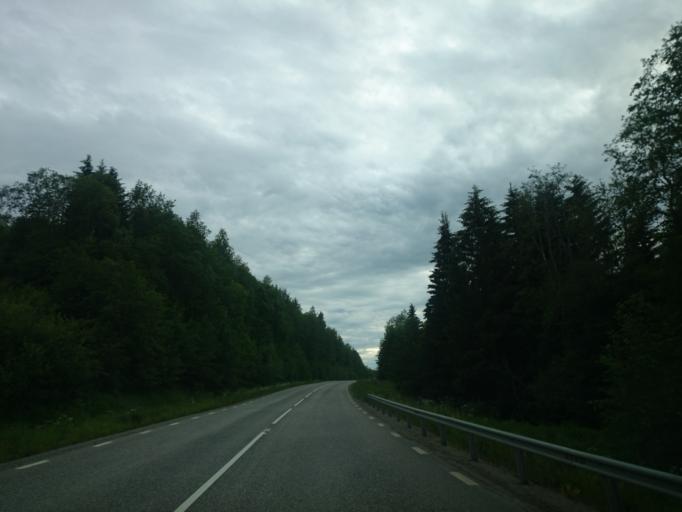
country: SE
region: Vaesternorrland
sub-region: Timra Kommun
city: Timra
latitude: 62.4688
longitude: 17.2926
